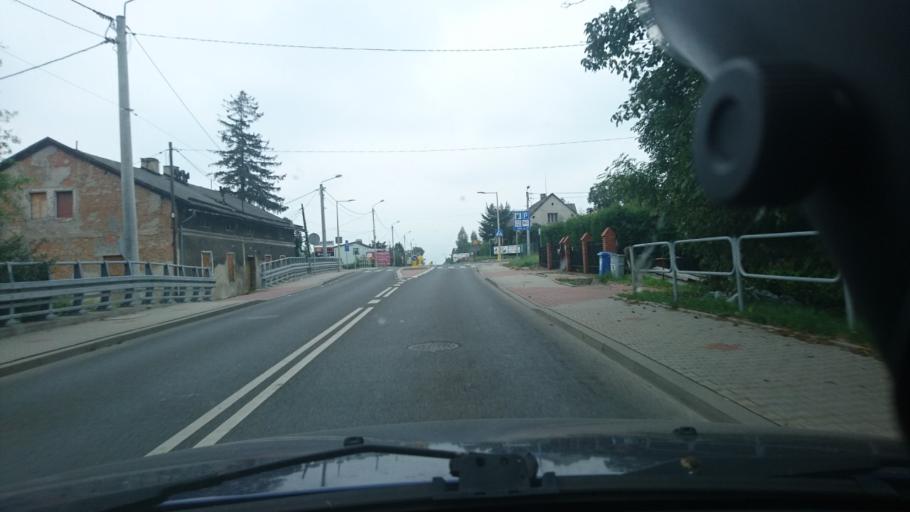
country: PL
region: Silesian Voivodeship
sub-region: Bielsko-Biala
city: Bielsko-Biala
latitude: 49.7960
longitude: 19.0645
